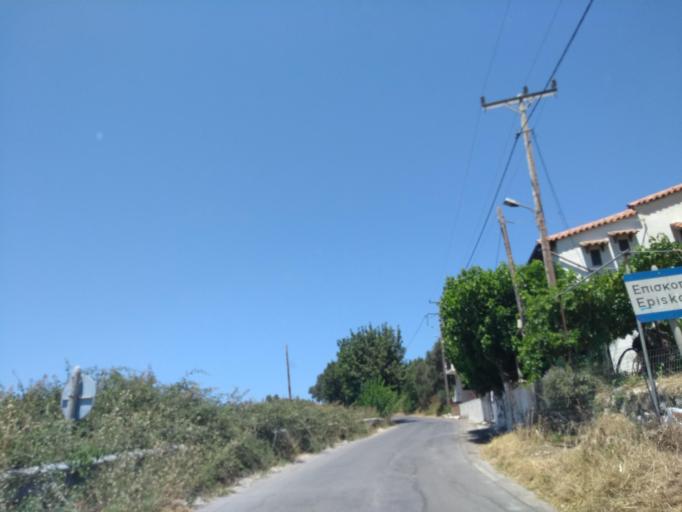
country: GR
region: Crete
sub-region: Nomos Chanias
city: Georgioupolis
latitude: 35.3263
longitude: 24.3340
